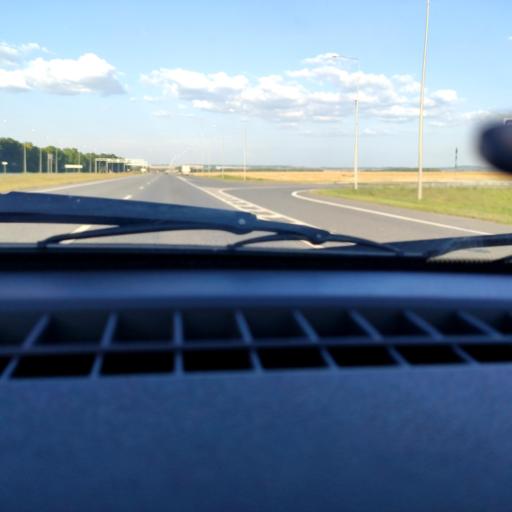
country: RU
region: Bashkortostan
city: Alekseyevka
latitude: 54.7241
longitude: 54.9233
